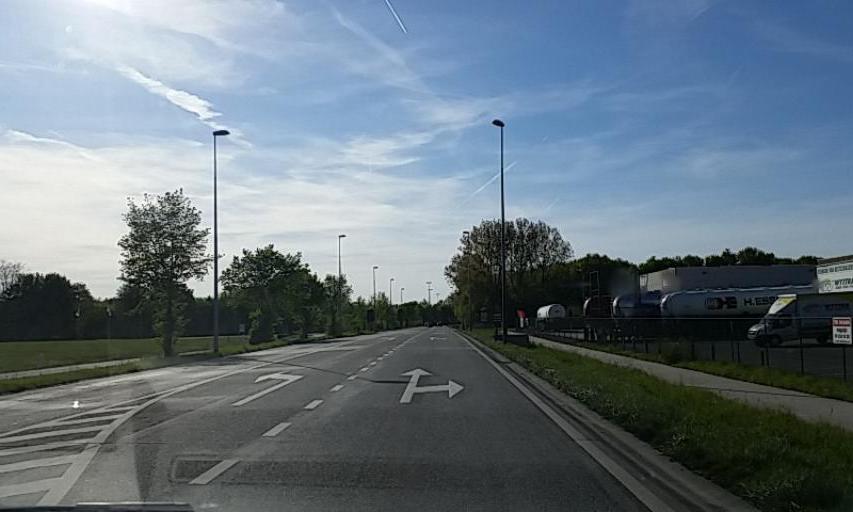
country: BE
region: Flanders
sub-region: Provincie Oost-Vlaanderen
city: Zelzate
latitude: 51.1881
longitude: 3.8293
